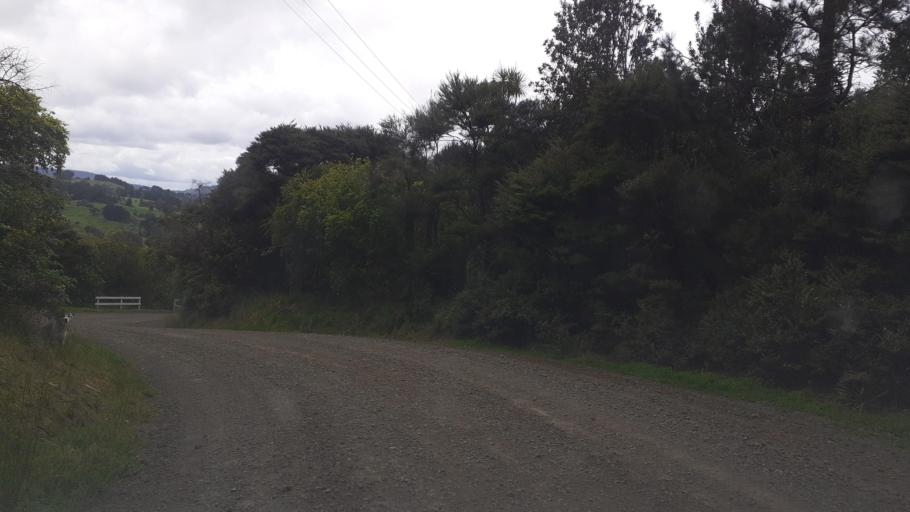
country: NZ
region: Northland
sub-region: Far North District
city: Kaitaia
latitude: -35.5292
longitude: 173.4294
